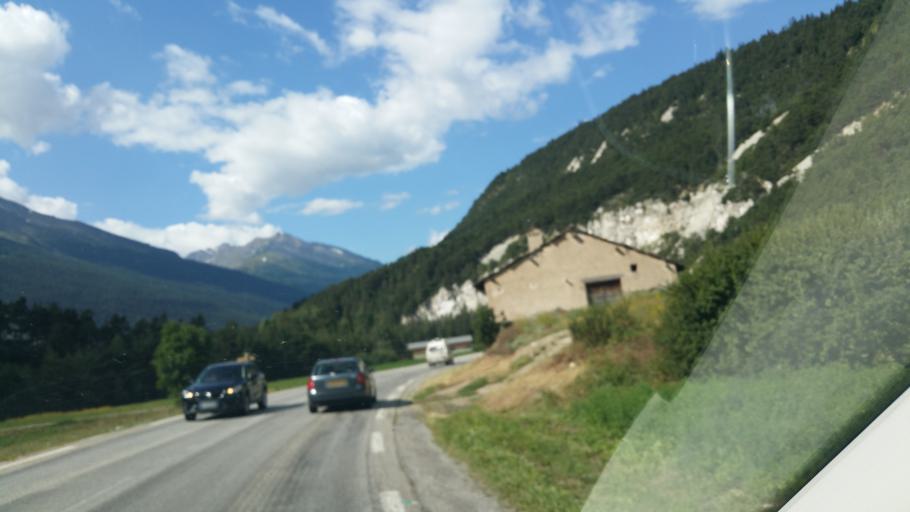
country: FR
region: Rhone-Alpes
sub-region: Departement de la Savoie
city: Modane
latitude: 45.2456
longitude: 6.7963
